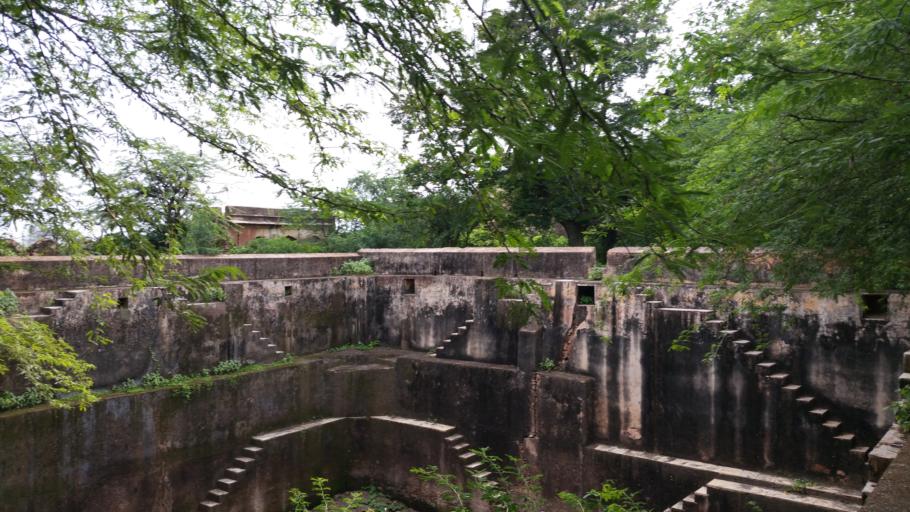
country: IN
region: Rajasthan
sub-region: Bundi
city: Bundi
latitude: 25.4511
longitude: 75.6366
